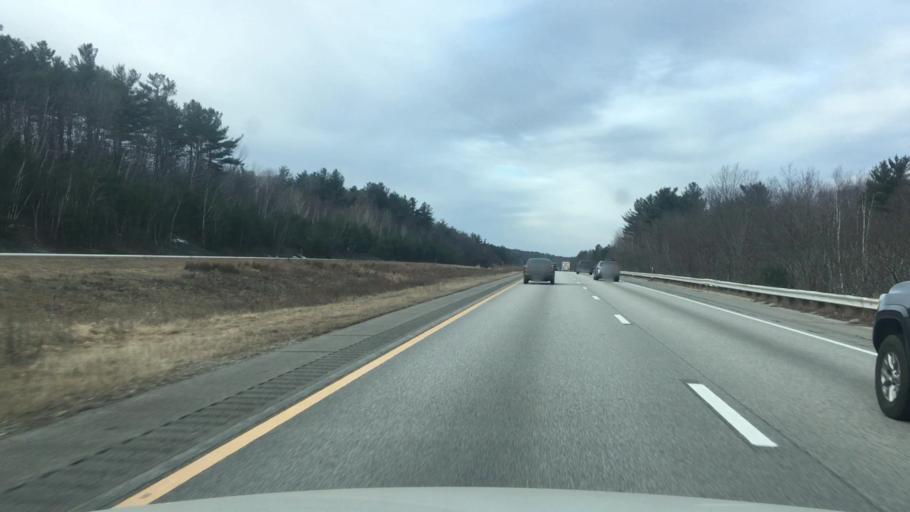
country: US
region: New Hampshire
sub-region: Rockingham County
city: Raymond
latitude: 43.0254
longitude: -71.2366
